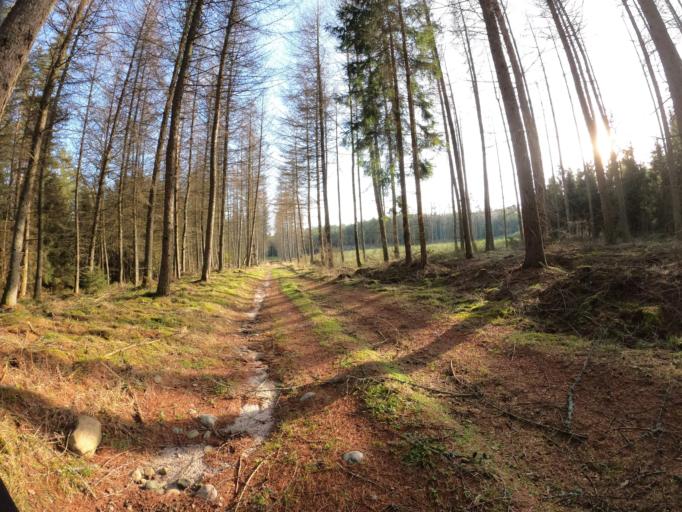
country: PL
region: West Pomeranian Voivodeship
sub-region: Powiat koszalinski
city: Polanow
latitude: 54.1897
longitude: 16.6717
